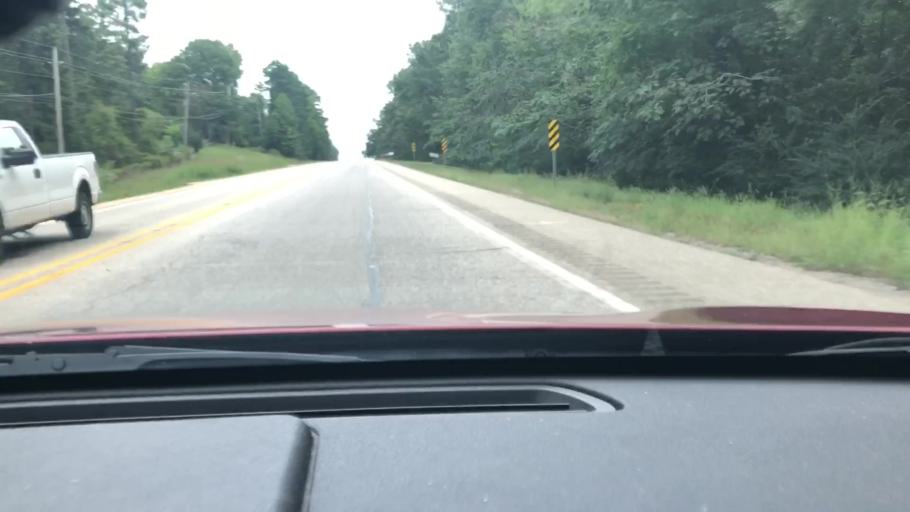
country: US
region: Arkansas
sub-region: Miller County
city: Texarkana
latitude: 33.4294
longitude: -93.9402
